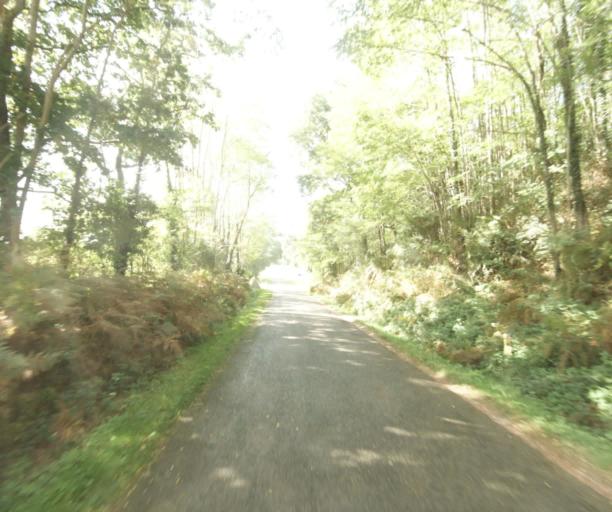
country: FR
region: Midi-Pyrenees
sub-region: Departement du Gers
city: Cazaubon
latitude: 43.9001
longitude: -0.1621
